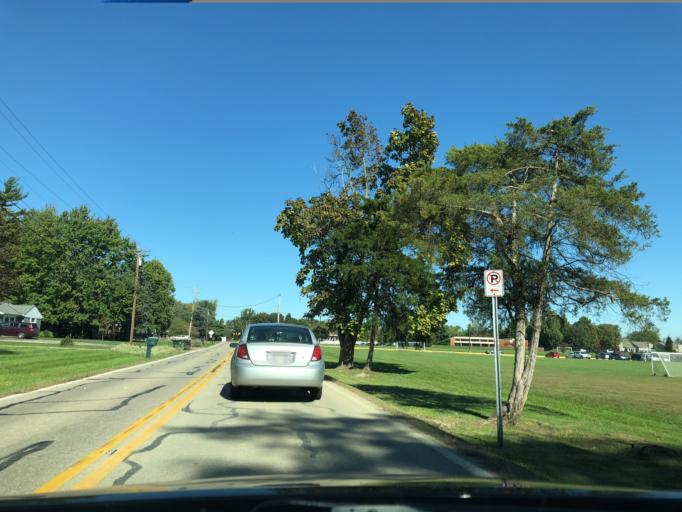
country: US
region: Ohio
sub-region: Hamilton County
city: Sixteen Mile Stand
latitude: 39.2822
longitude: -84.3105
